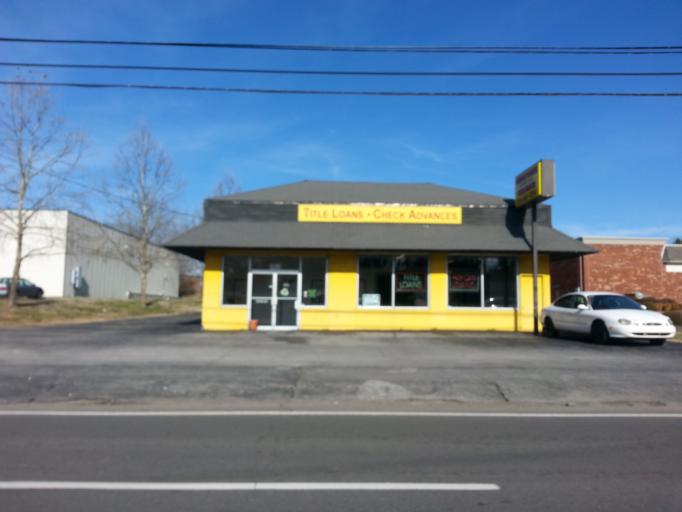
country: US
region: Tennessee
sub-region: Rutherford County
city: Murfreesboro
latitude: 35.8380
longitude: -86.3858
